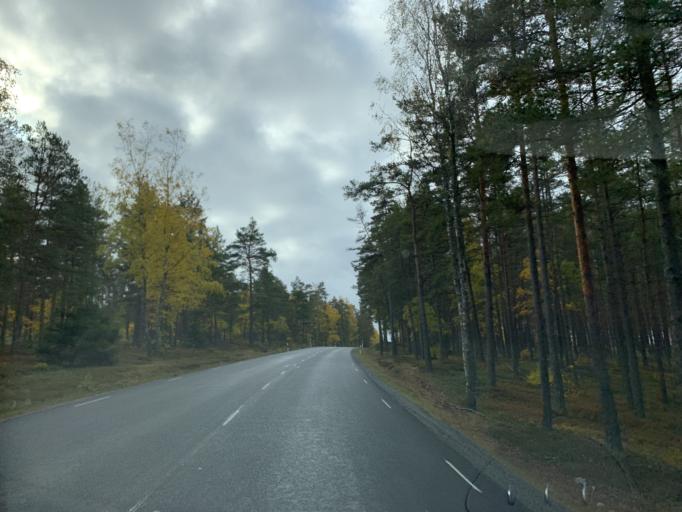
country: SE
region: Stockholm
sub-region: Botkyrka Kommun
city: Varsta
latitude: 59.0788
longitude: 17.7871
